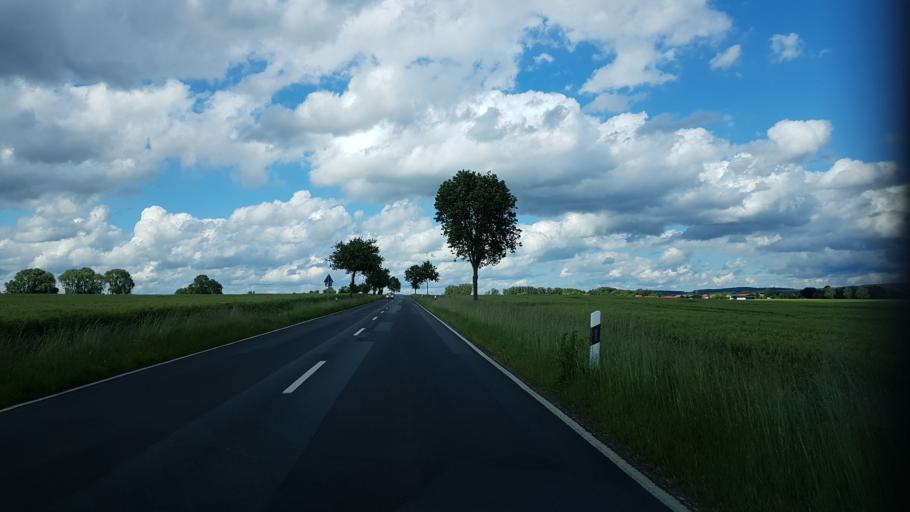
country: DE
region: Lower Saxony
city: Hardegsen
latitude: 51.6299
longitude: 9.8542
